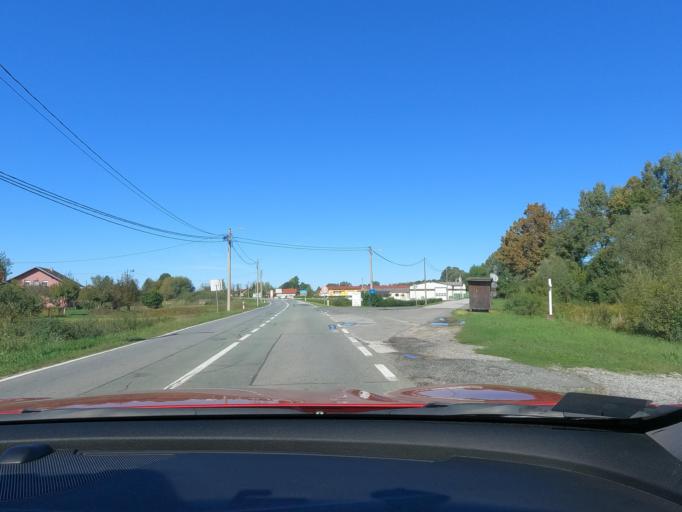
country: HR
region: Sisacko-Moslavacka
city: Budasevo
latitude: 45.4899
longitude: 16.4560
